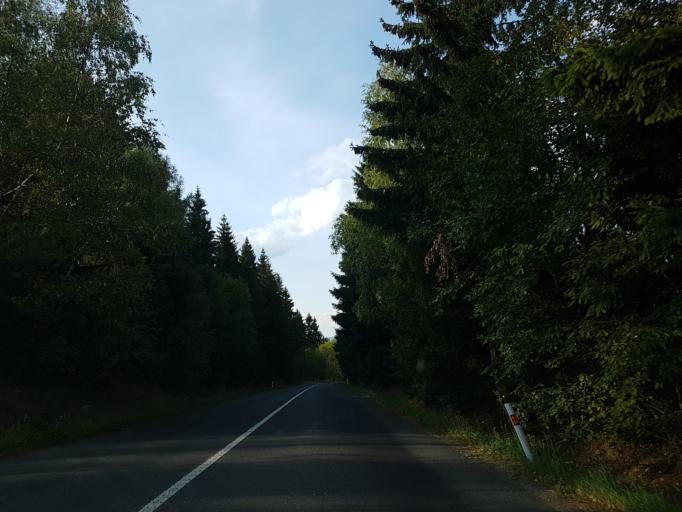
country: CZ
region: Liberecky
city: Mala Skala
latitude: 50.6629
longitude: 15.1683
